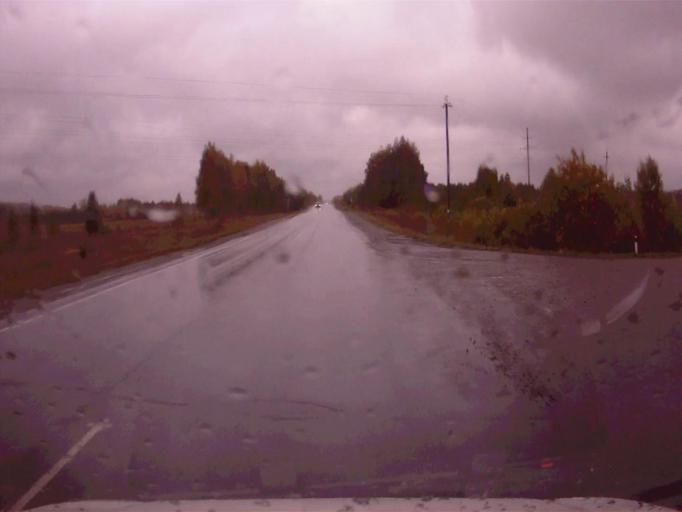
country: RU
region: Chelyabinsk
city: Argayash
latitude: 55.4778
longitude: 60.8513
